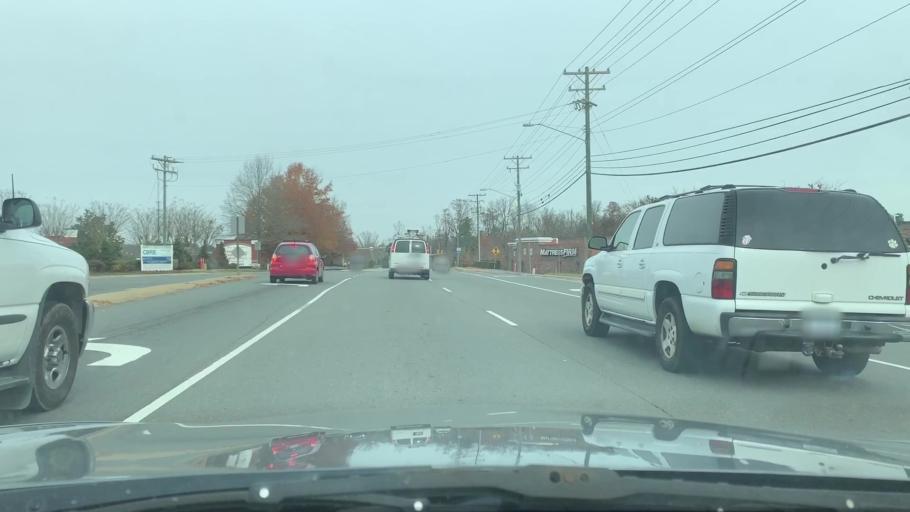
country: US
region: North Carolina
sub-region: Orange County
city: Chapel Hill
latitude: 35.9539
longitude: -78.9943
